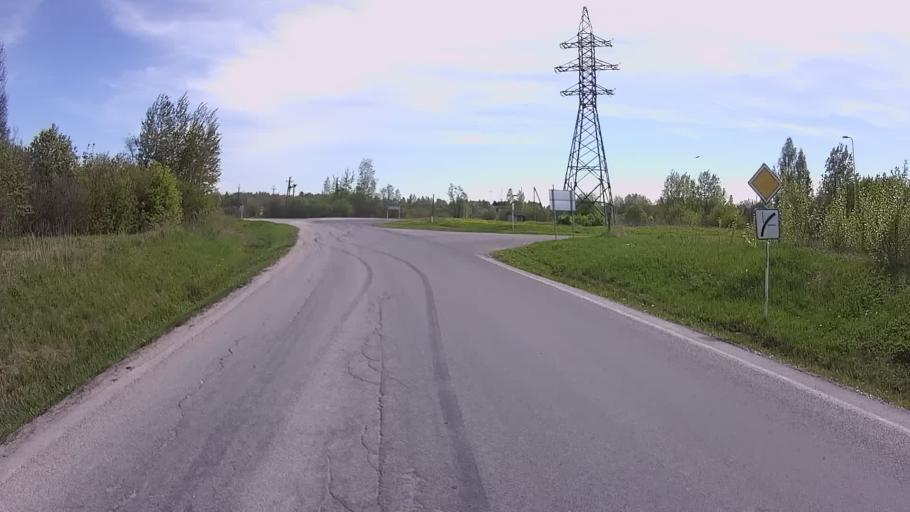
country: EE
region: Valgamaa
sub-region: Valga linn
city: Valga
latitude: 57.7753
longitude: 26.0726
